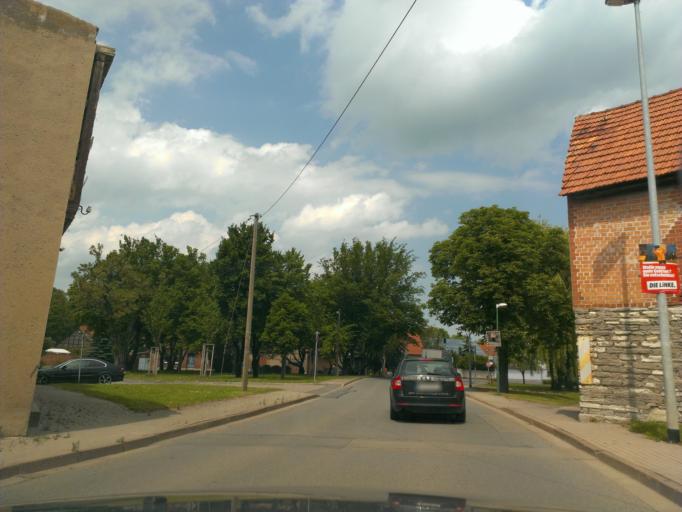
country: DE
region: Thuringia
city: Kleinmolsen
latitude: 51.0164
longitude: 11.1157
